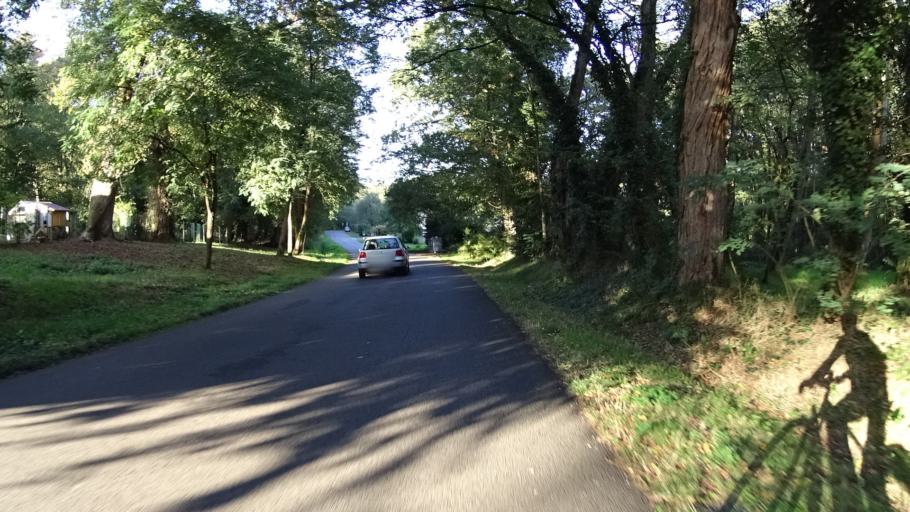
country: FR
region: Aquitaine
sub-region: Departement des Landes
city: Saint-Paul-les-Dax
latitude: 43.7357
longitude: -1.0437
